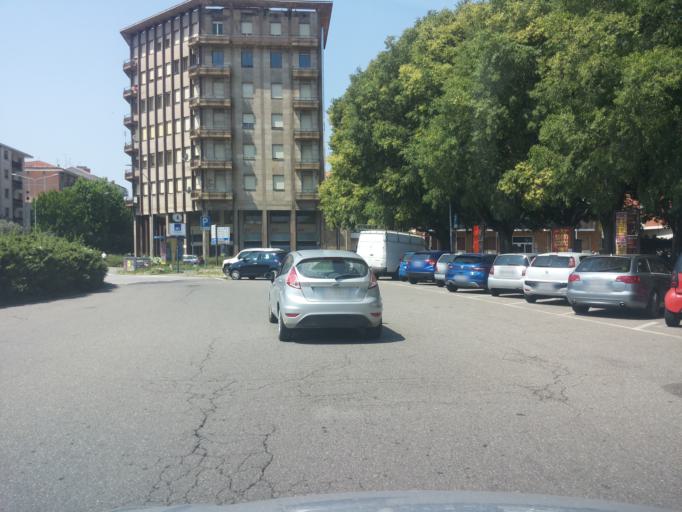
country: IT
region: Piedmont
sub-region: Provincia di Biella
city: Biella
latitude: 45.5572
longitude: 8.0667
